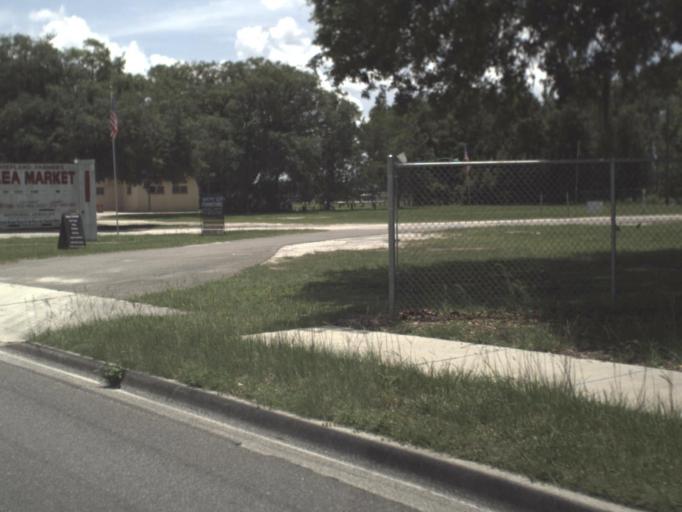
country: US
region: Florida
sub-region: Levy County
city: Chiefland
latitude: 29.4910
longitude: -82.8633
